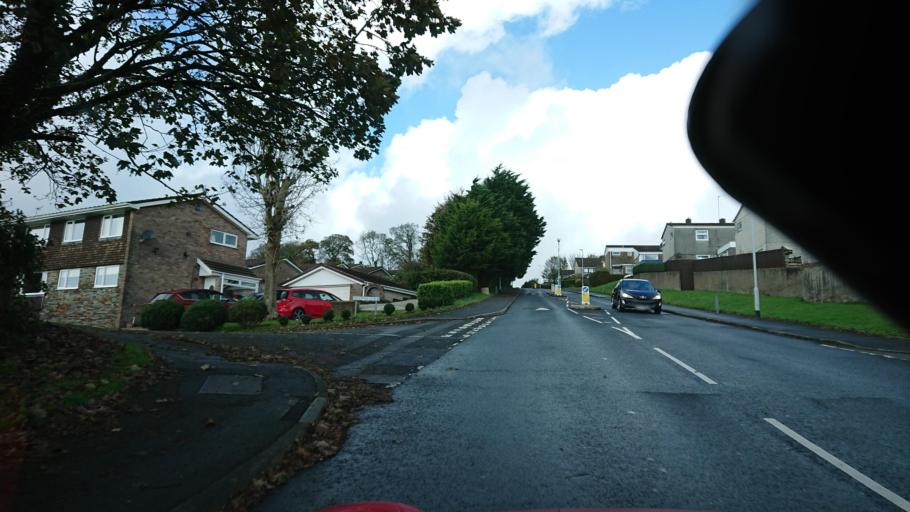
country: GB
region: England
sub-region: Plymouth
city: Plymouth
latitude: 50.4009
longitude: -4.1263
